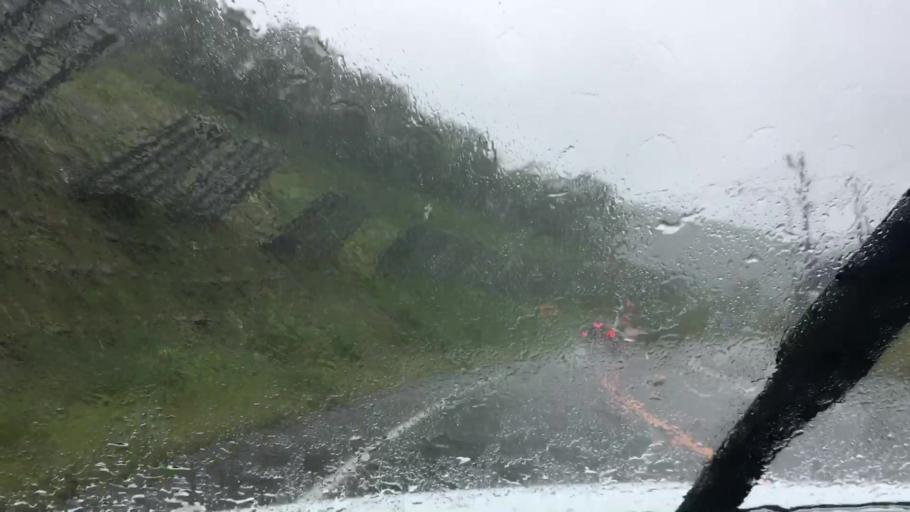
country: JP
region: Hokkaido
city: Sapporo
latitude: 42.8468
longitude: 141.0822
